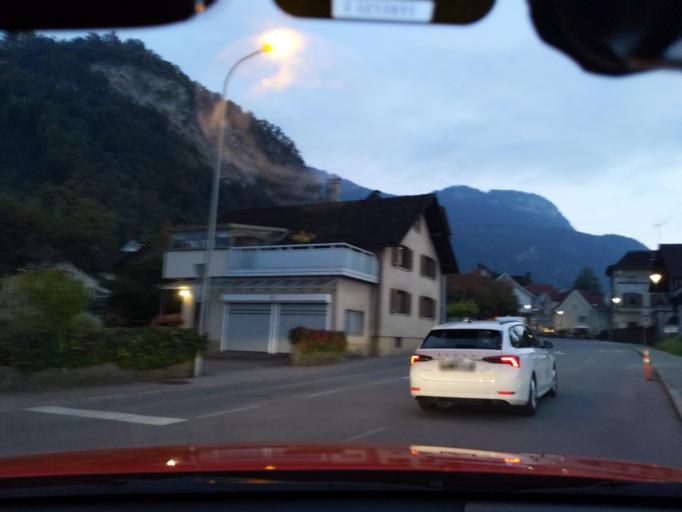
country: AT
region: Vorarlberg
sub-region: Politischer Bezirk Dornbirn
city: Hohenems
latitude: 47.3672
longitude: 9.6893
